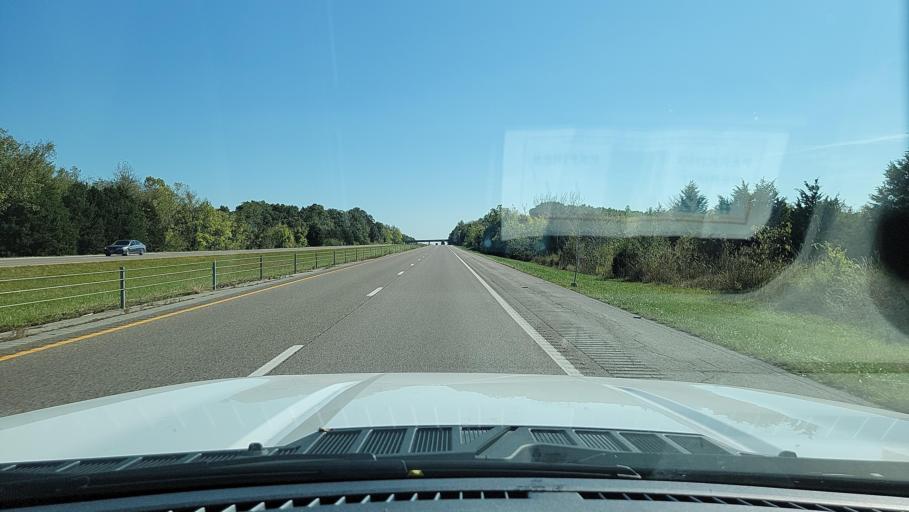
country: US
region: Missouri
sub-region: Jefferson County
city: Crystal City
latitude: 38.1155
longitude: -90.3085
